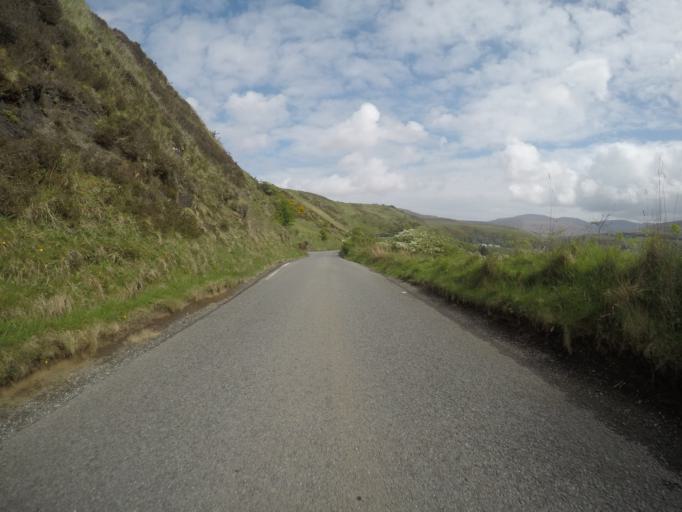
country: GB
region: Scotland
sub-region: Highland
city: Portree
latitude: 57.5918
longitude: -6.3756
